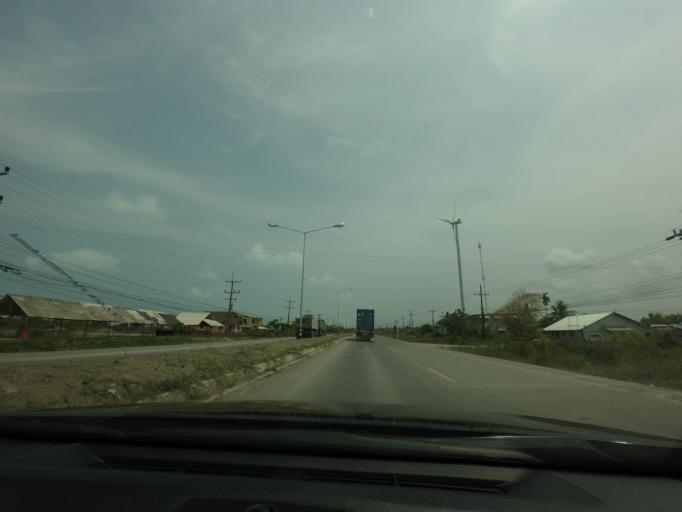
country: TH
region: Nakhon Si Thammarat
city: Hua Sai
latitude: 7.9166
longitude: 100.3366
